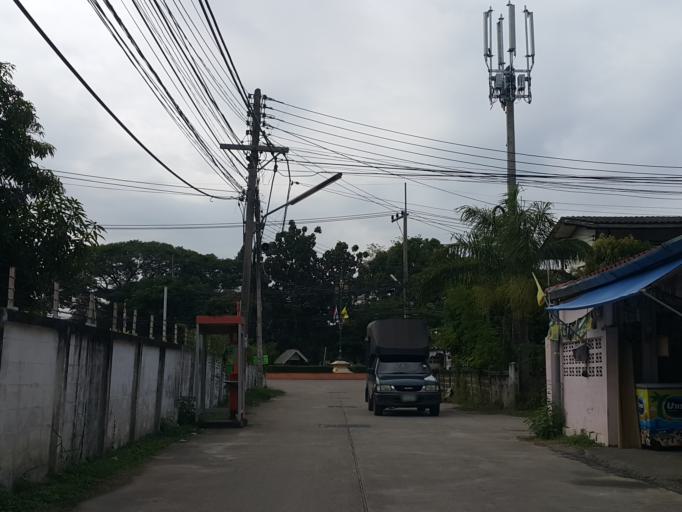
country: TH
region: Lampang
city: Lampang
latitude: 18.2996
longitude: 99.4934
